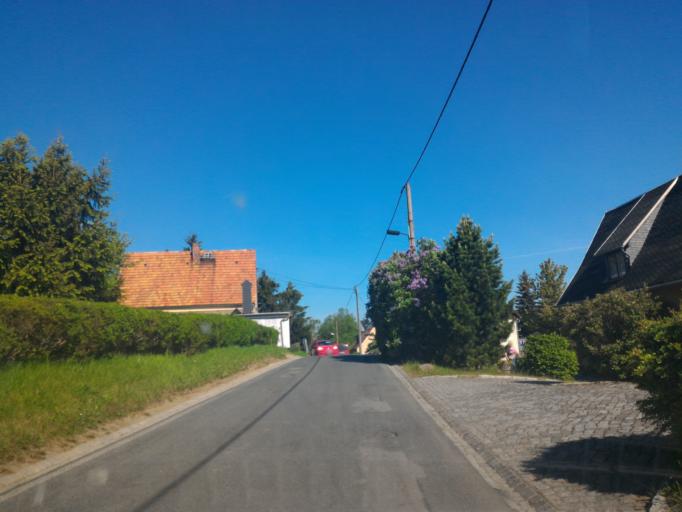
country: DE
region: Saxony
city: Durrhennersdorf
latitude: 51.0293
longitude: 14.6292
